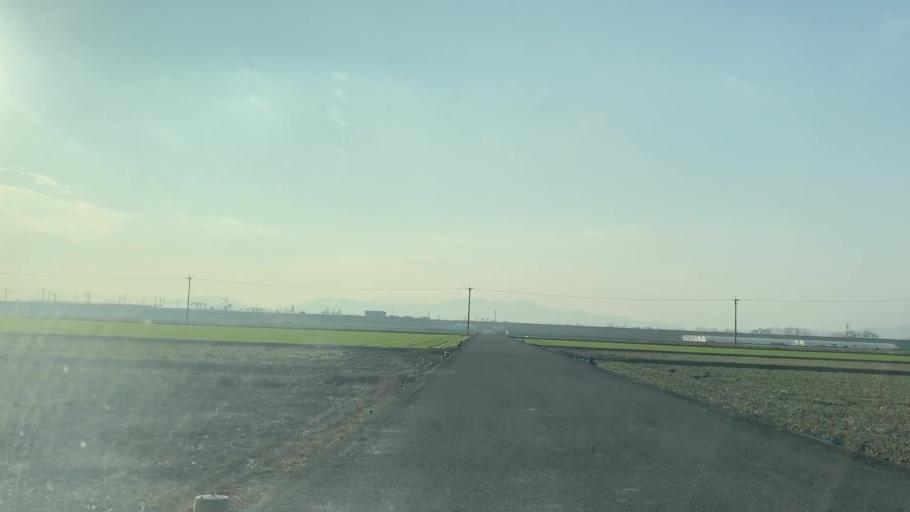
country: JP
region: Saga Prefecture
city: Saga-shi
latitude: 33.2600
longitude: 130.2500
